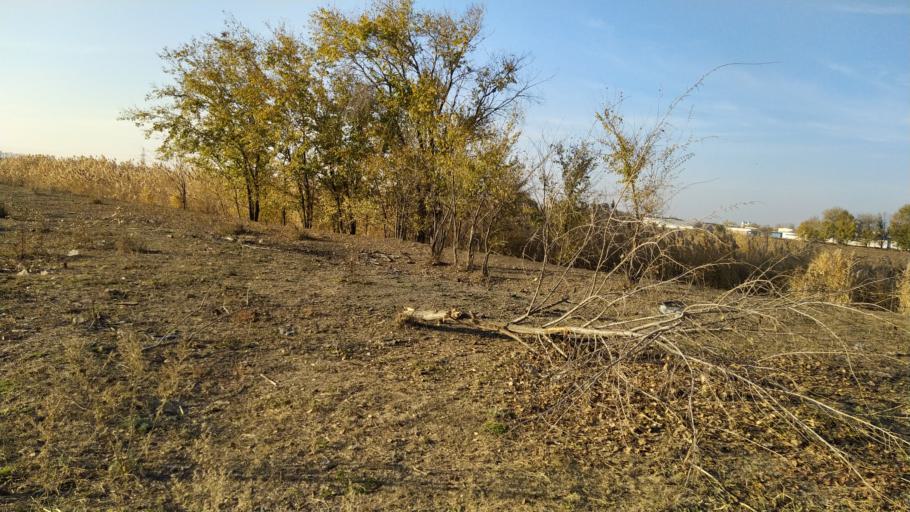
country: RU
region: Rostov
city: Bataysk
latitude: 47.1213
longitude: 39.7221
